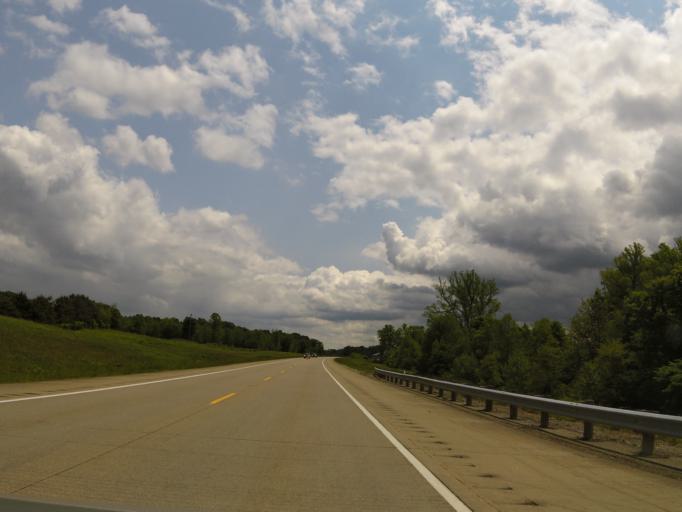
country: US
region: West Virginia
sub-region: Mason County
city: New Haven
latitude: 39.0089
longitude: -81.9055
